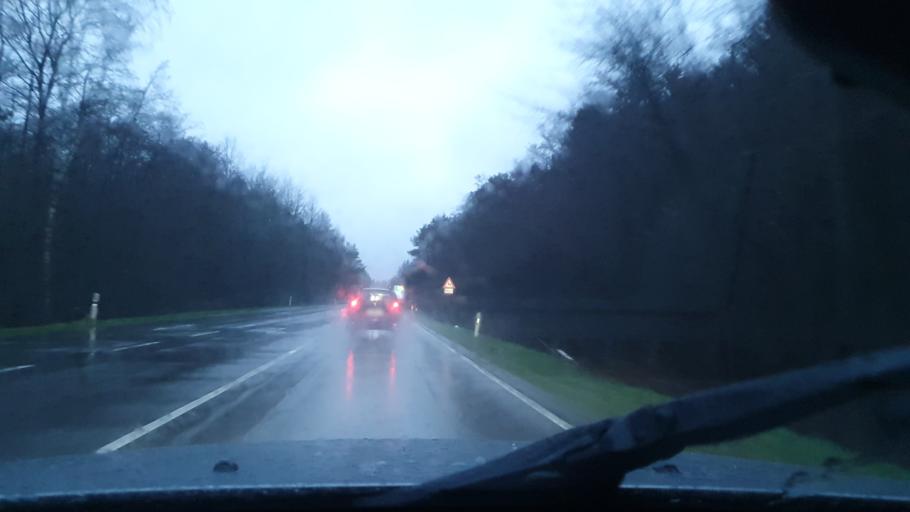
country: DE
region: Rheinland-Pfalz
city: Bechhofen
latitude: 49.3671
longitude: 7.3765
